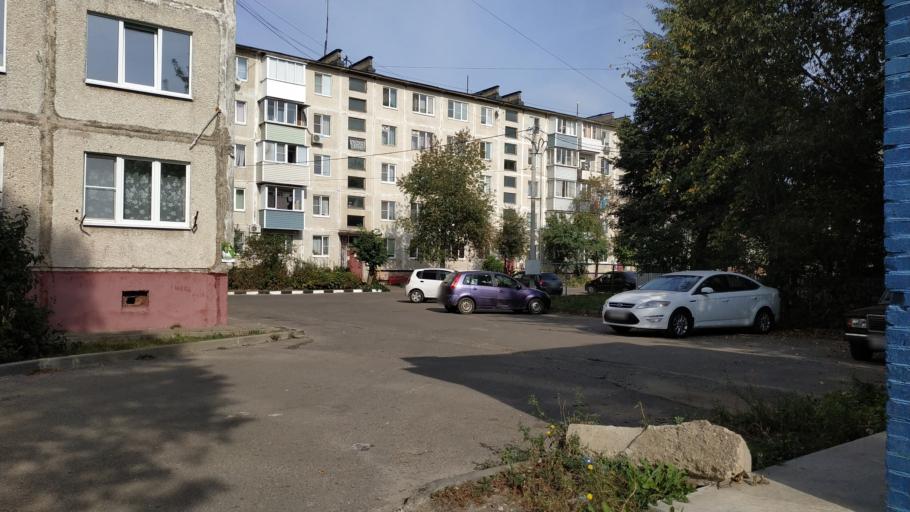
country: RU
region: Moskovskaya
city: Bronnitsy
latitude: 55.4221
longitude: 38.2876
